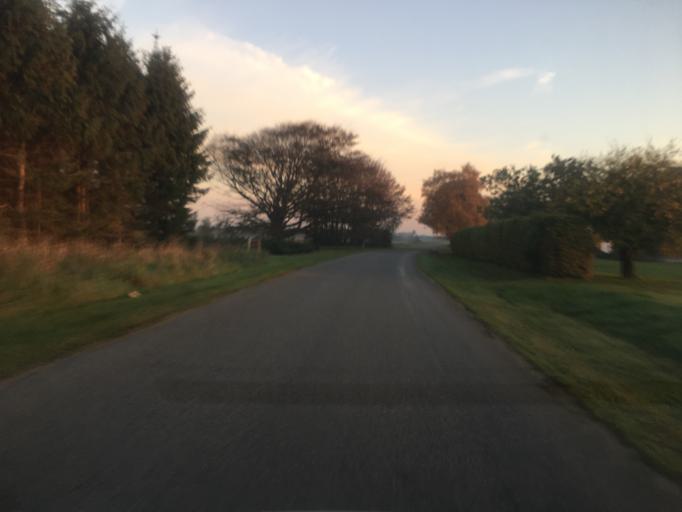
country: DK
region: South Denmark
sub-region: Tonder Kommune
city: Logumkloster
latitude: 55.0213
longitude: 9.0452
